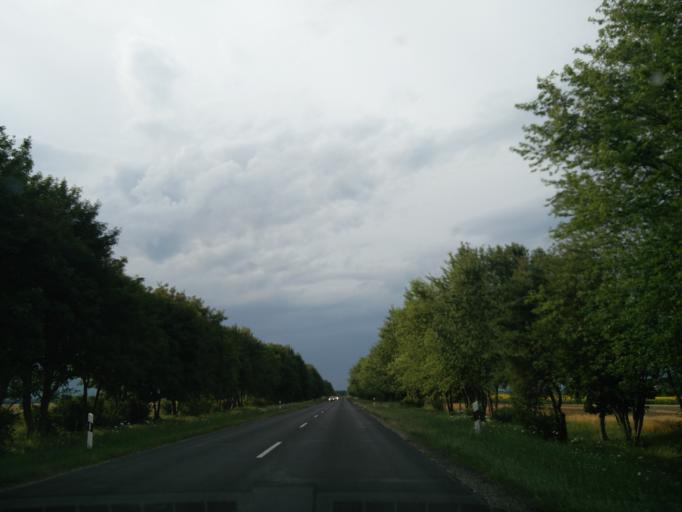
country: HU
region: Vas
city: Vasvar
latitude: 46.9901
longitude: 16.8315
